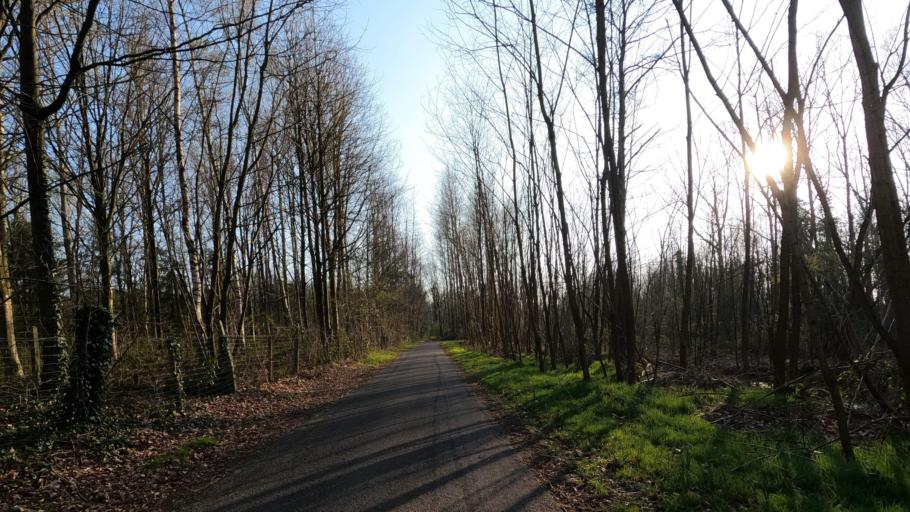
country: BE
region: Flanders
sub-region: Provincie Antwerpen
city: Rijkevorsel
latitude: 51.3307
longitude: 4.7971
